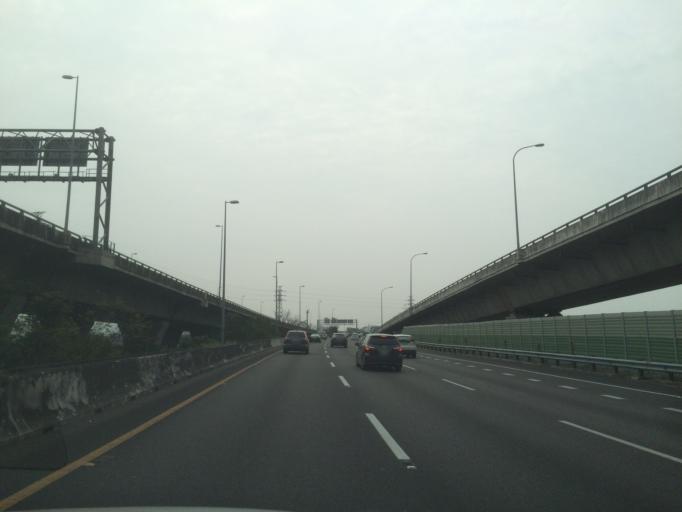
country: TW
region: Taiwan
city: Zhongxing New Village
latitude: 24.0463
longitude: 120.6790
